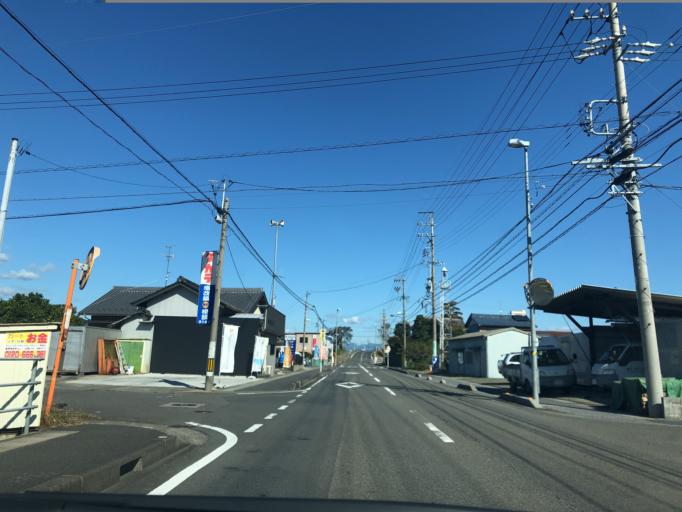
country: JP
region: Gifu
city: Ogaki
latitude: 35.3740
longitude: 136.6676
